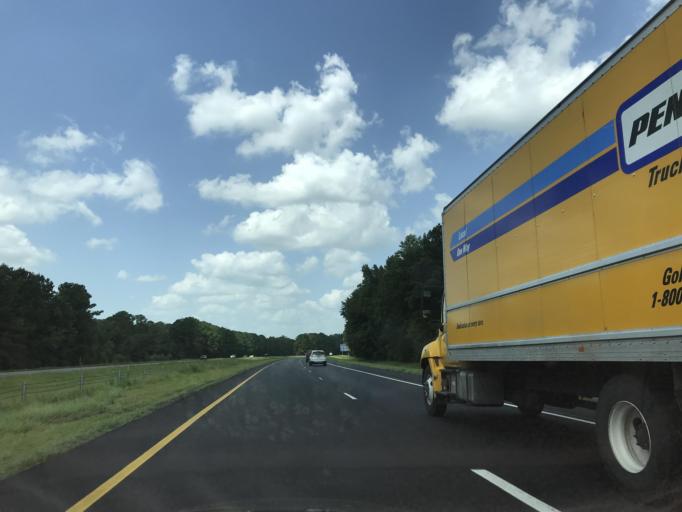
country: US
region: North Carolina
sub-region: Duplin County
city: Warsaw
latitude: 34.9771
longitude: -78.1266
